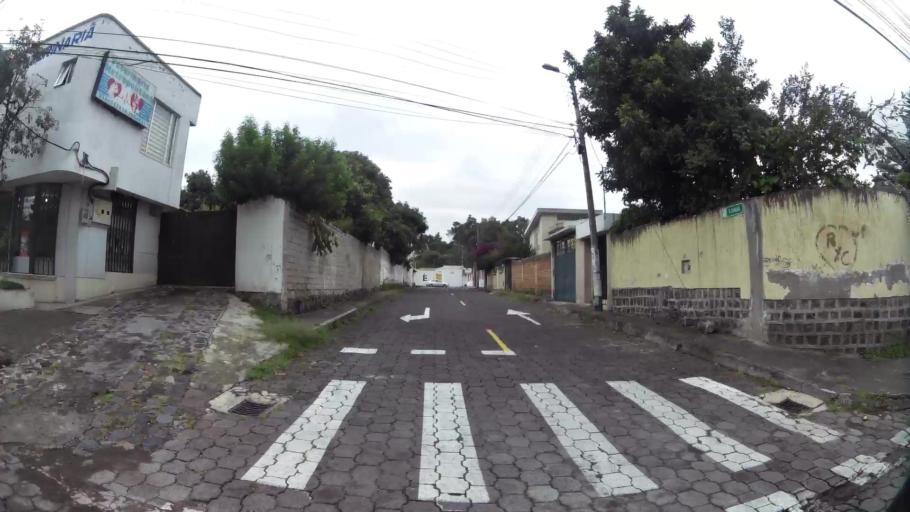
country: EC
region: Pichincha
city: Sangolqui
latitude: -0.3043
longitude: -78.4594
